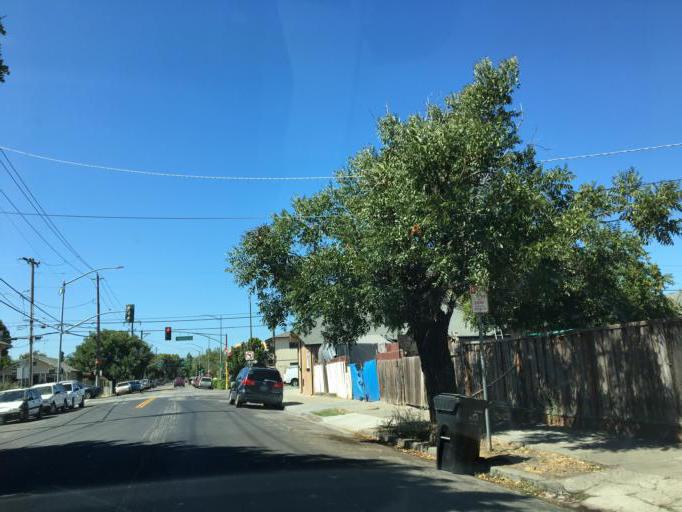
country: US
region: California
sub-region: Santa Clara County
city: San Jose
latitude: 37.3179
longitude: -121.8807
